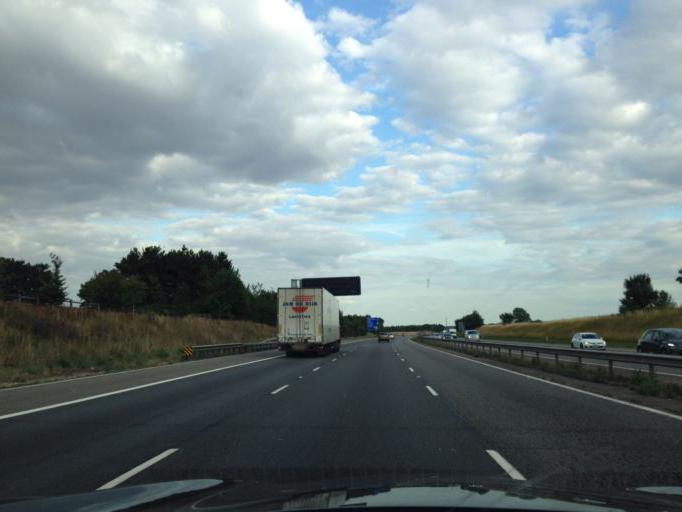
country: GB
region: England
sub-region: Oxfordshire
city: Somerton
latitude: 51.9629
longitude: -1.2246
